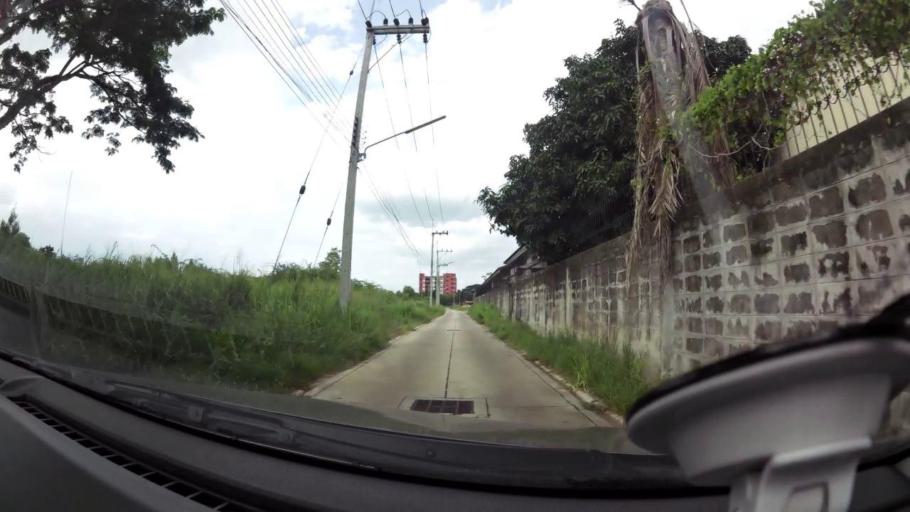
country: TH
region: Prachuap Khiri Khan
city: Hua Hin
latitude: 12.6228
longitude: 99.9486
